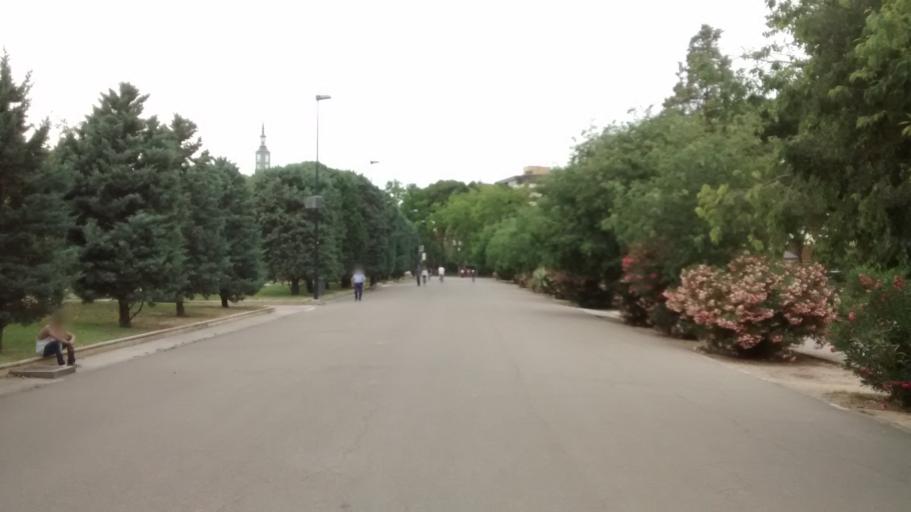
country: ES
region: Aragon
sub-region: Provincia de Zaragoza
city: Delicias
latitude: 41.6357
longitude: -0.8954
